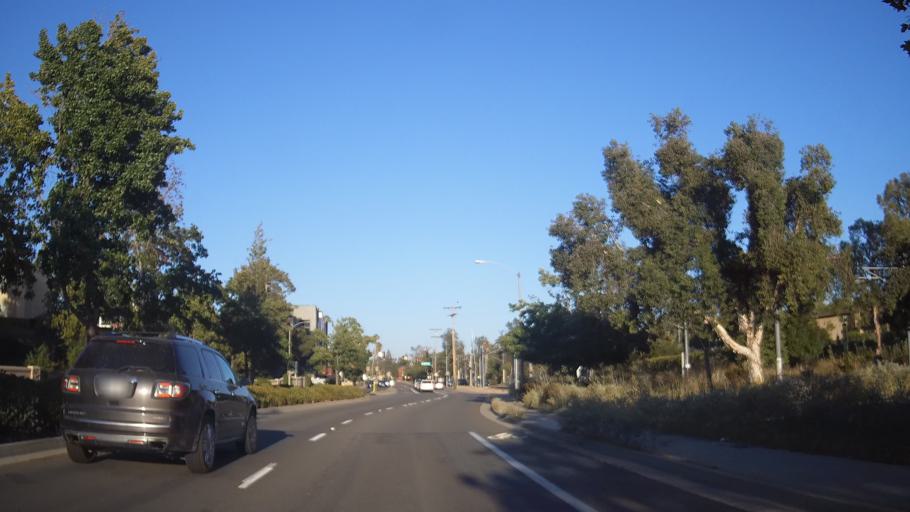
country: US
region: California
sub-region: San Diego County
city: La Mesa
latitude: 32.7860
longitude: -117.0004
